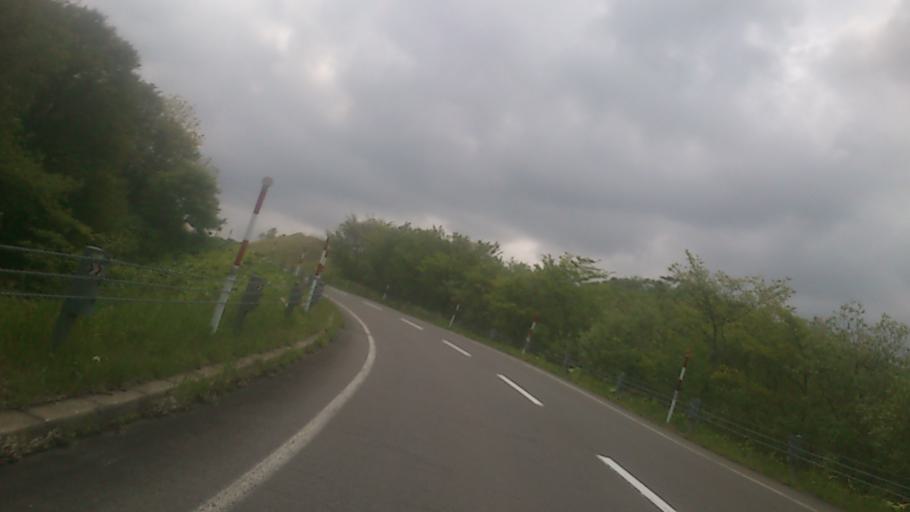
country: JP
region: Hokkaido
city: Nemuro
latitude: 43.1474
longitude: 145.1394
